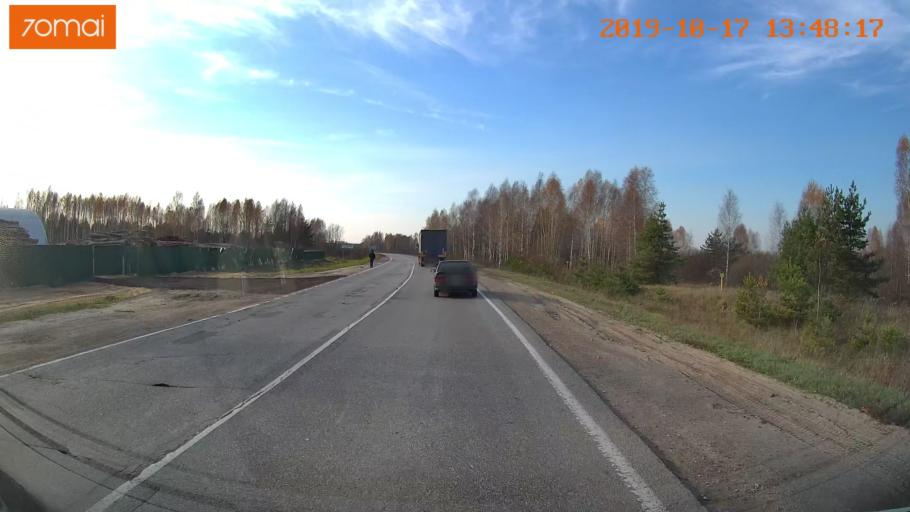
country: RU
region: Rjazan
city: Tuma
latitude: 55.1473
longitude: 40.4589
